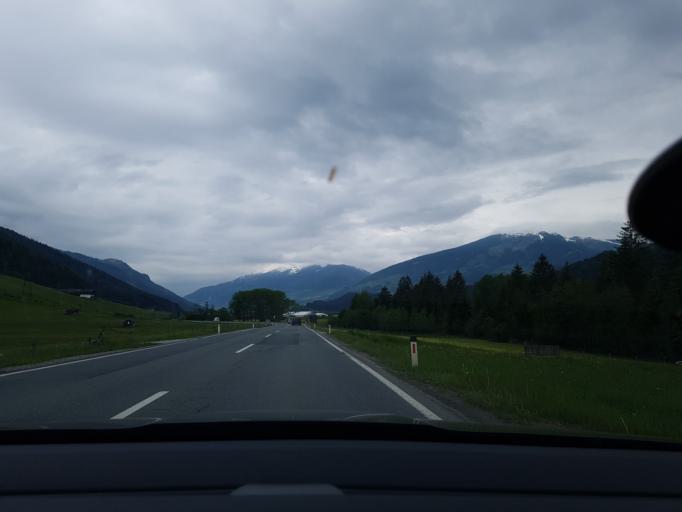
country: AT
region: Salzburg
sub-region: Politischer Bezirk Zell am See
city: Mittersill
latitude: 47.2778
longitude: 12.4666
